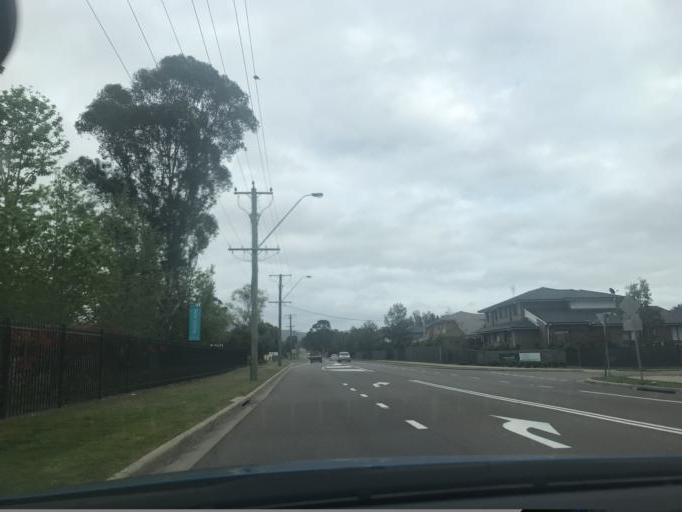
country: AU
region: New South Wales
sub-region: Cessnock
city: Cessnock
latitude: -32.8306
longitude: 151.3392
